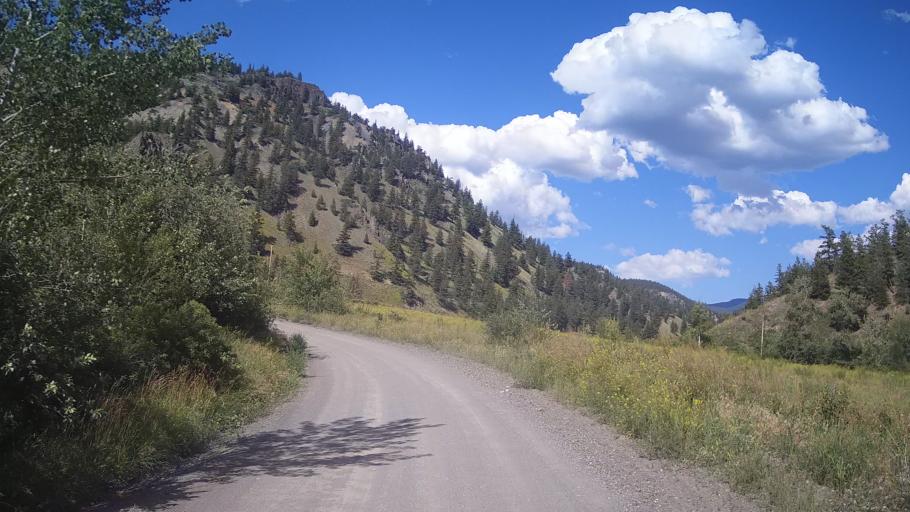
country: CA
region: British Columbia
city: Lillooet
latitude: 51.2433
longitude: -122.0385
